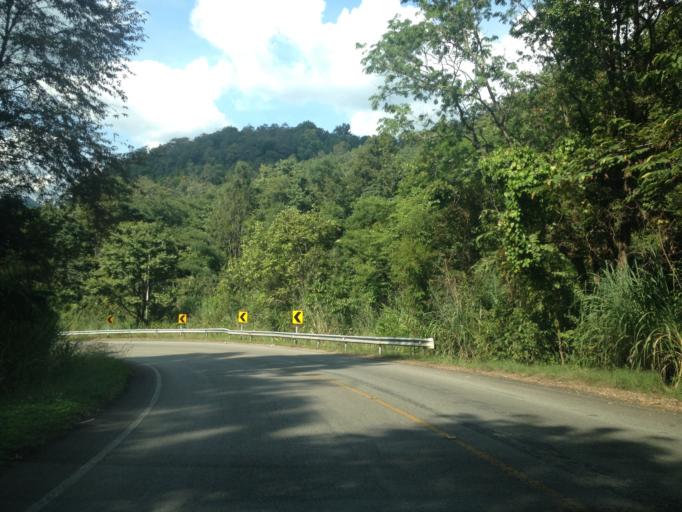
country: TH
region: Chiang Mai
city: Samoeng
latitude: 18.8056
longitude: 98.8077
